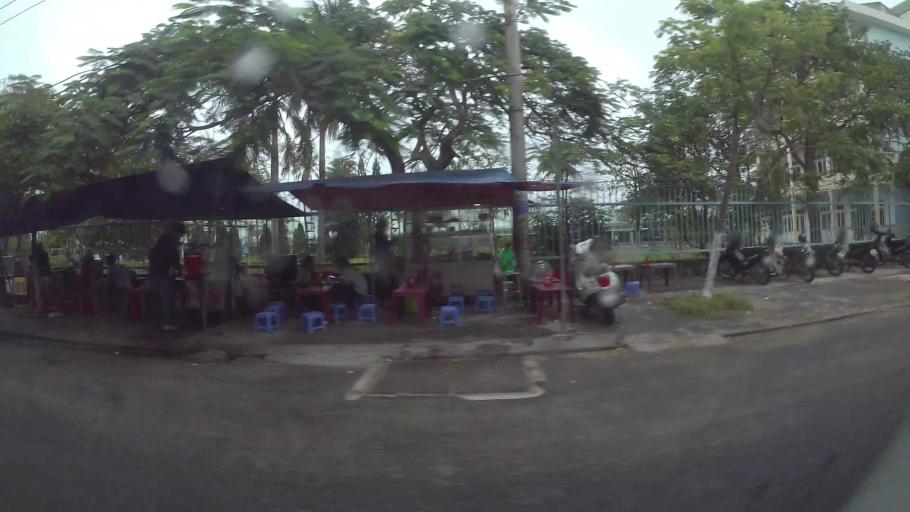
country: VN
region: Da Nang
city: Da Nang
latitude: 16.0769
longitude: 108.2131
